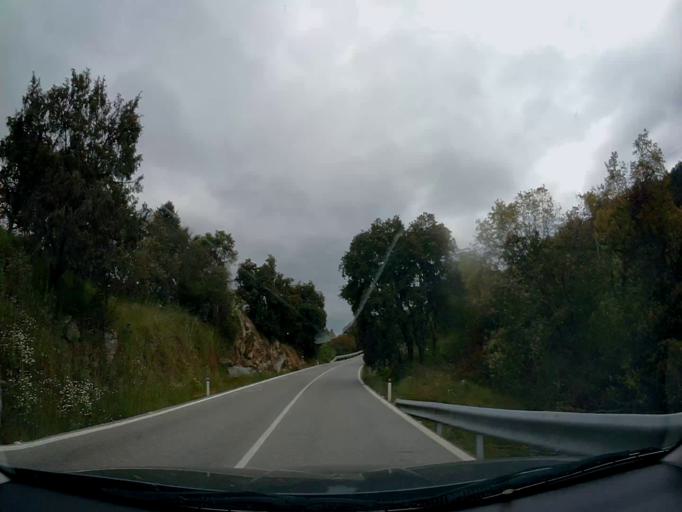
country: ES
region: Madrid
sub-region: Provincia de Madrid
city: Navalagamella
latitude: 40.4464
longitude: -4.1159
